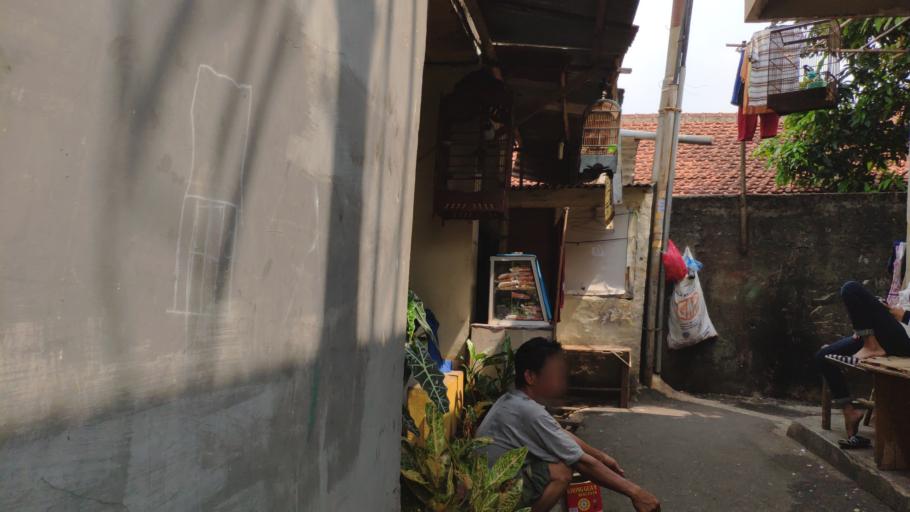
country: ID
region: Banten
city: South Tangerang
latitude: -6.2693
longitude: 106.7728
